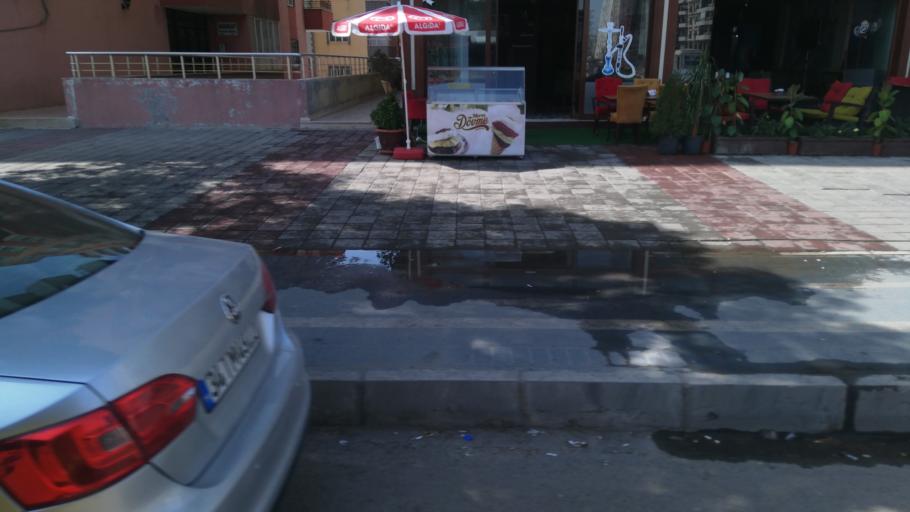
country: TR
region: Mardin
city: Midyat
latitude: 37.4214
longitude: 41.3487
